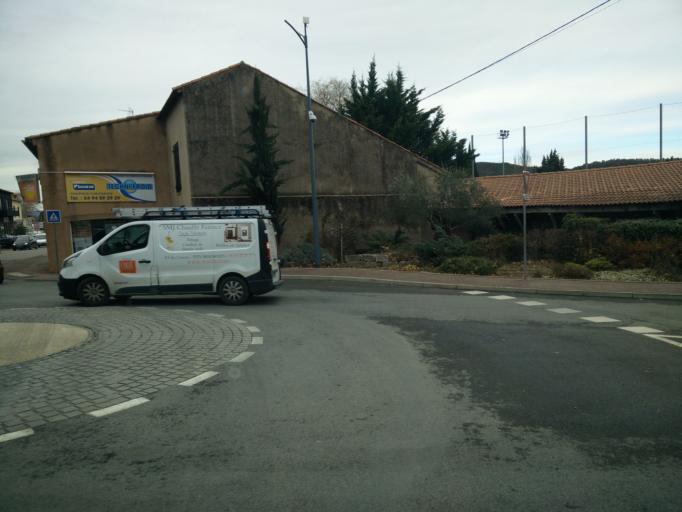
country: FR
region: Provence-Alpes-Cote d'Azur
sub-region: Departement du Var
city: Brignoles
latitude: 43.4074
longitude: 6.0540
